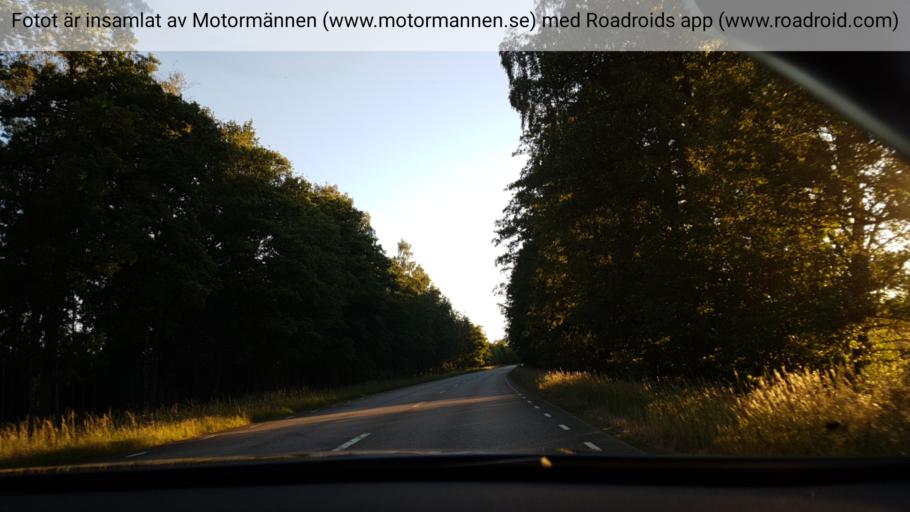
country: SE
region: Vaestra Goetaland
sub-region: Hjo Kommun
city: Hjo
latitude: 58.3216
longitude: 14.3001
